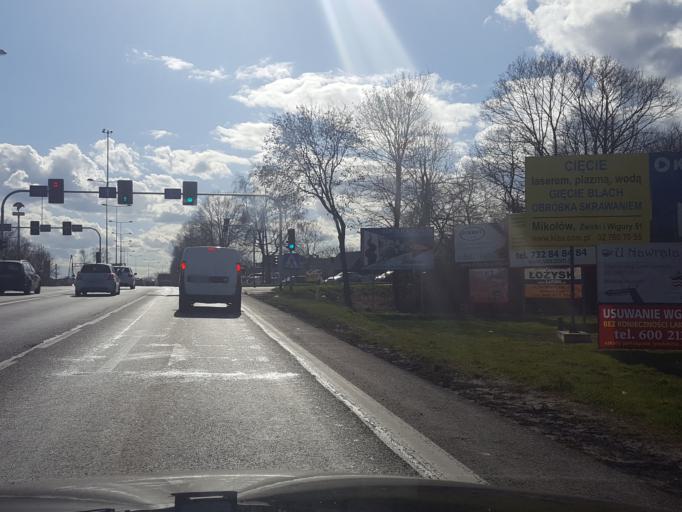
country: PL
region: Silesian Voivodeship
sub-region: Powiat mikolowski
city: Mikolow
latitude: 50.1724
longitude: 18.8722
